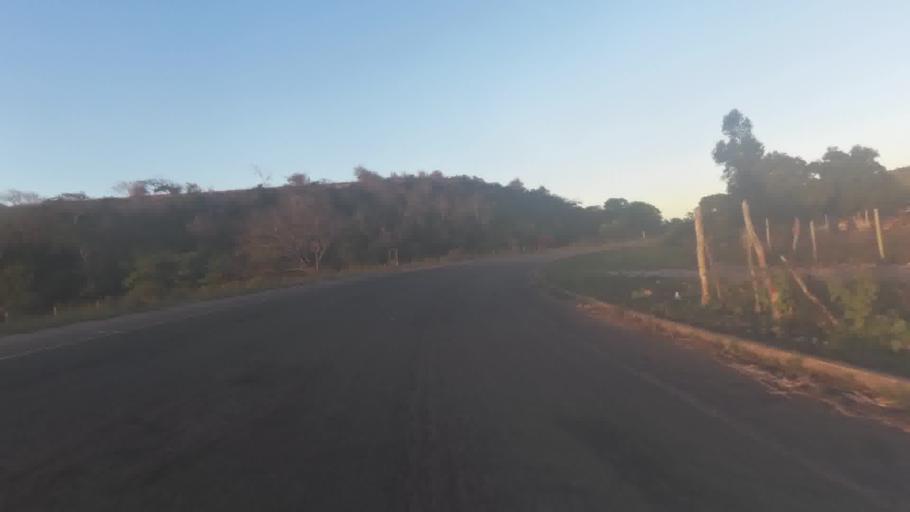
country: BR
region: Espirito Santo
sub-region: Marataizes
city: Marataizes
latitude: -21.1852
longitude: -40.9317
